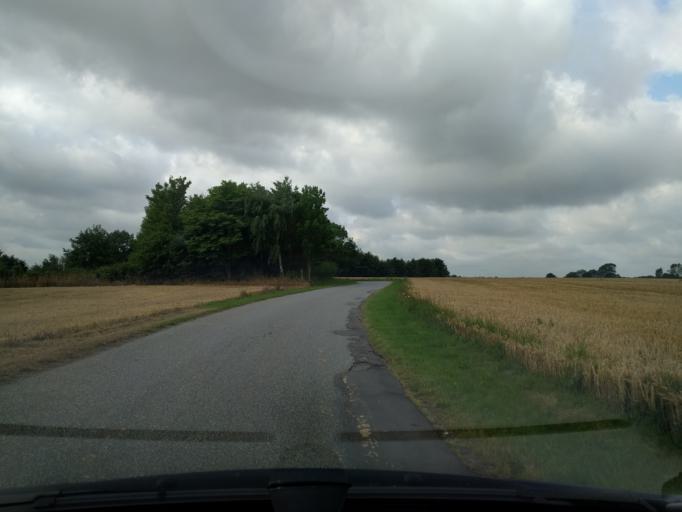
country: DK
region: Zealand
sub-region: Guldborgsund Kommune
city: Stubbekobing
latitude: 54.9022
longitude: 11.9844
